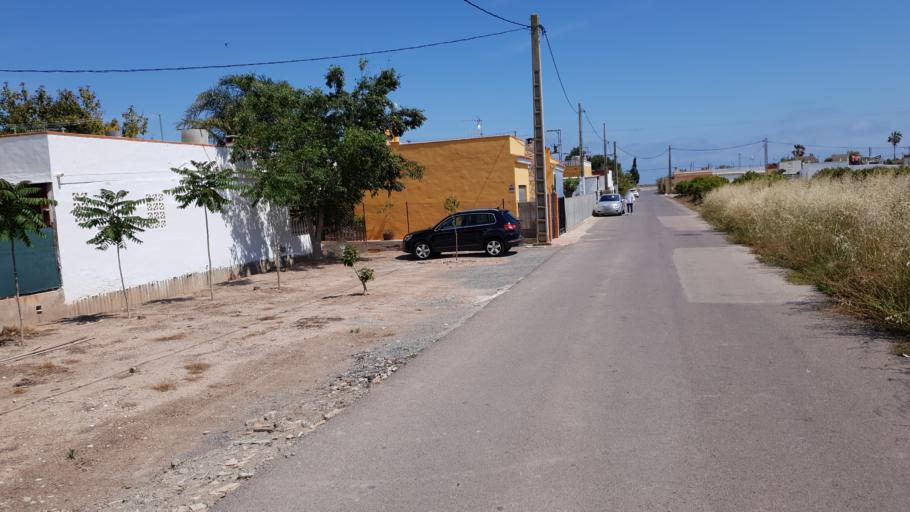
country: ES
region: Valencia
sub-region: Provincia de Castello
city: Burriana
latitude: 39.8592
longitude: -0.0877
